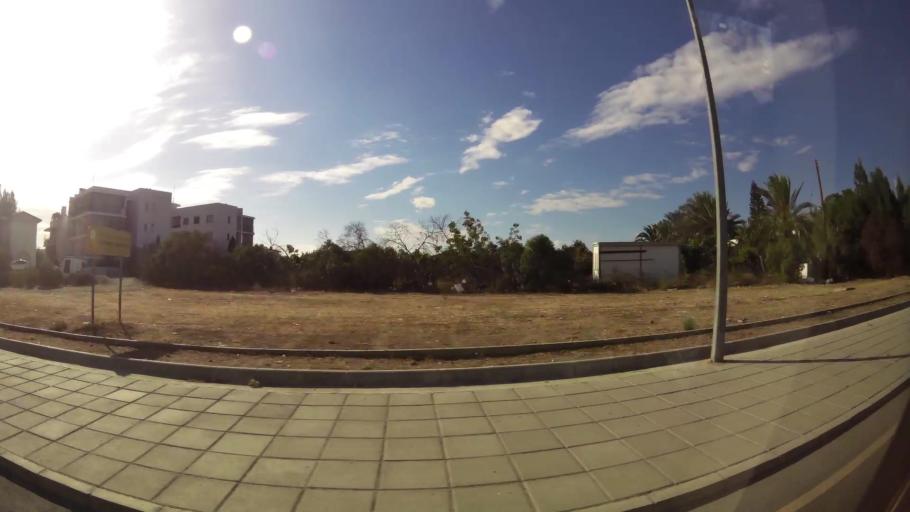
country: CY
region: Lefkosia
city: Nicosia
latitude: 35.1350
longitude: 33.3598
